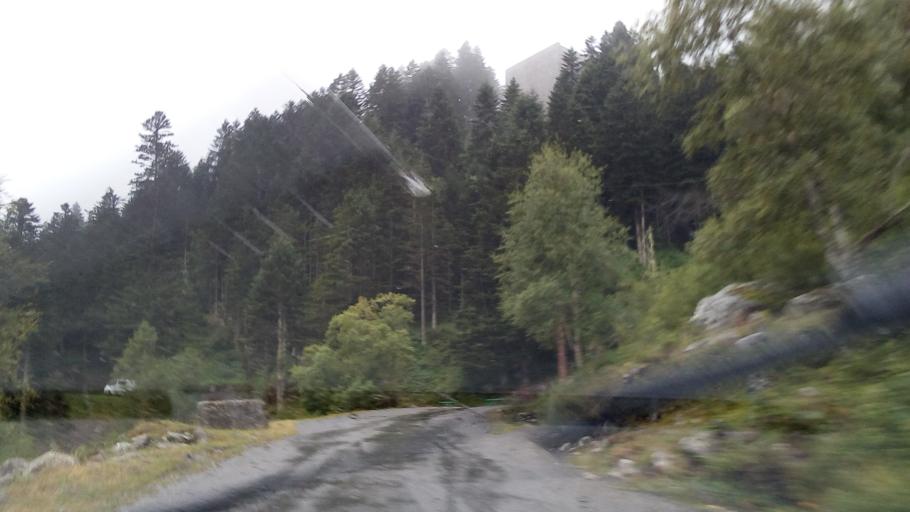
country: ES
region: Aragon
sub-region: Provincia de Huesca
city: Sallent de Gallego
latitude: 42.8886
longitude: -0.2713
